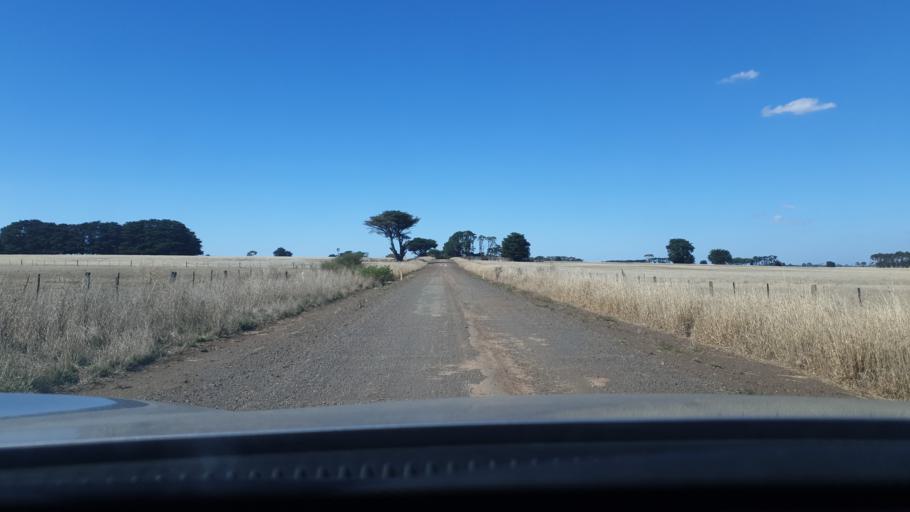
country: AU
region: Victoria
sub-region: Warrnambool
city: Warrnambool
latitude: -38.1649
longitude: 142.3814
